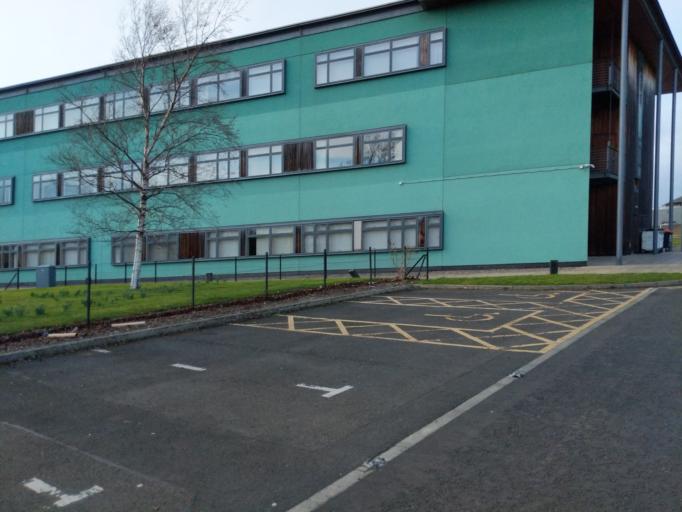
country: GB
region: Scotland
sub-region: Edinburgh
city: Currie
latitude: 55.9297
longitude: -3.2982
